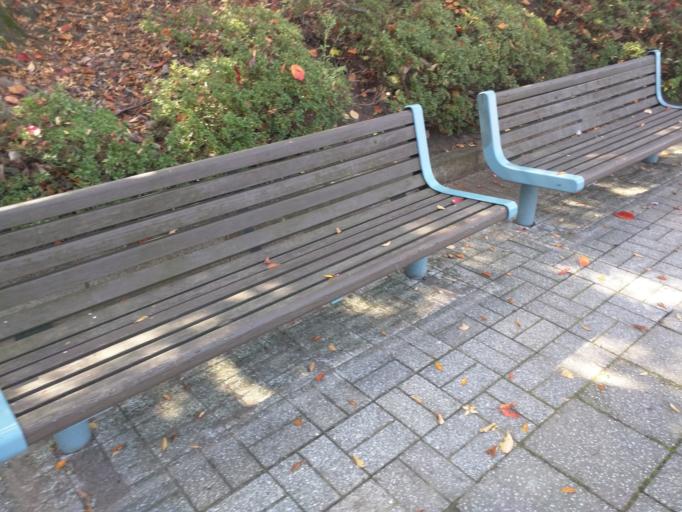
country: JP
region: Fukushima
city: Kitakata
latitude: 37.4618
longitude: 139.9232
